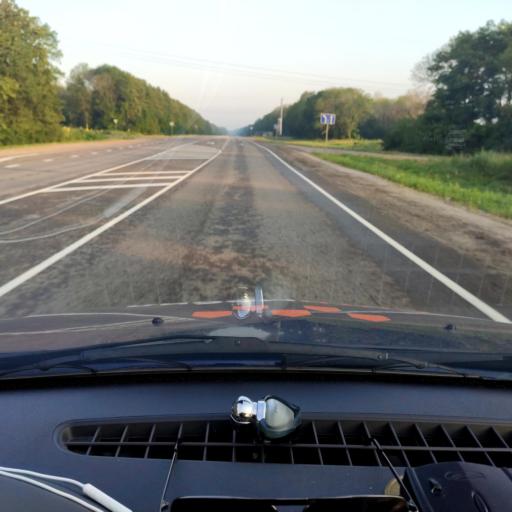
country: RU
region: Lipetsk
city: Yelets
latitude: 52.5662
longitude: 38.6726
